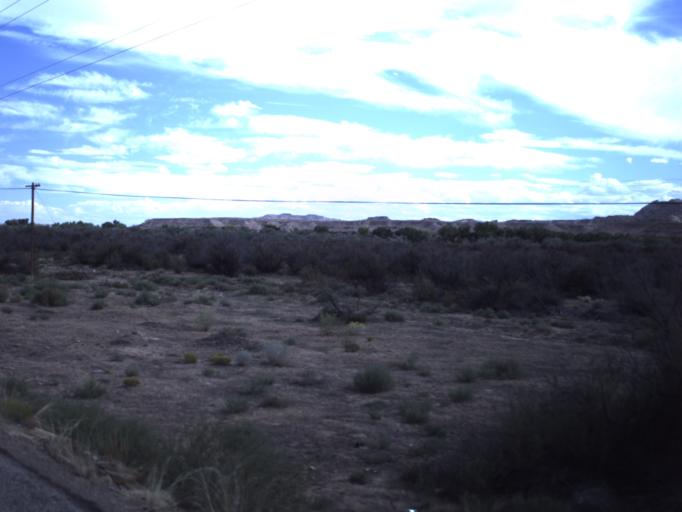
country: US
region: Colorado
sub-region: Montezuma County
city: Towaoc
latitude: 37.2204
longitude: -109.1983
